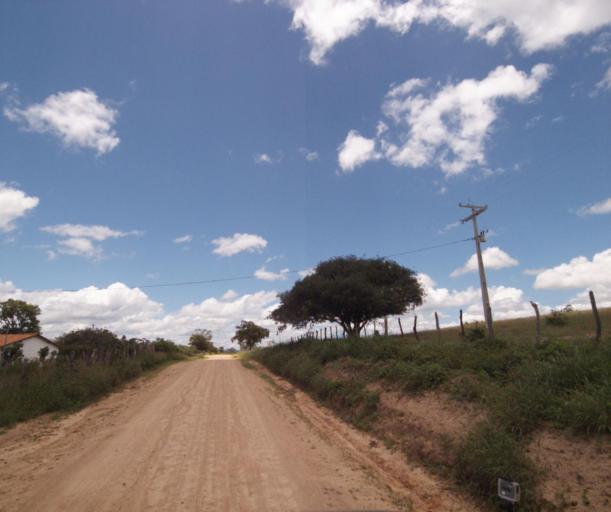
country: BR
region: Bahia
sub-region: Pocoes
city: Pocoes
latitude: -14.3811
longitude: -40.3659
